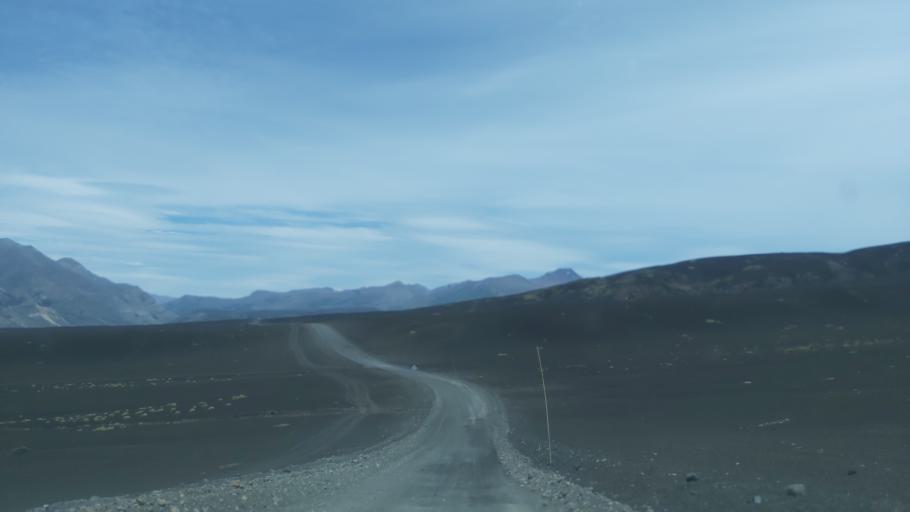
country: AR
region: Neuquen
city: Andacollo
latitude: -37.4225
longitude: -71.2876
